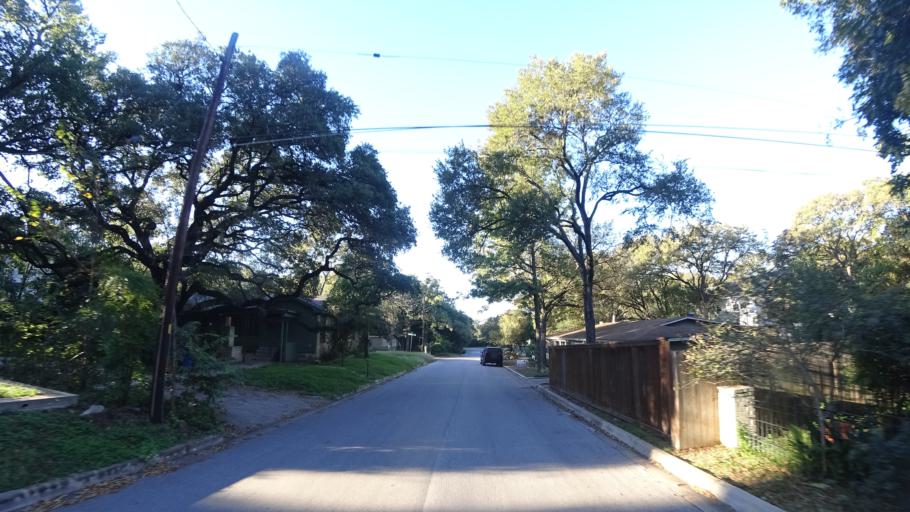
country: US
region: Texas
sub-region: Travis County
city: Rollingwood
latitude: 30.2935
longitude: -97.7747
